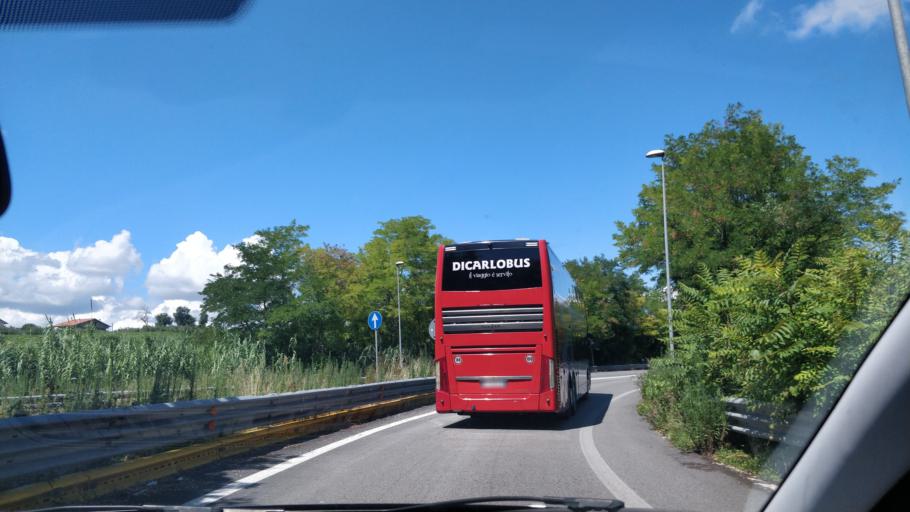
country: IT
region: Abruzzo
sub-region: Provincia di Chieti
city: Francavilla al Mare
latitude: 42.4059
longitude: 14.3021
